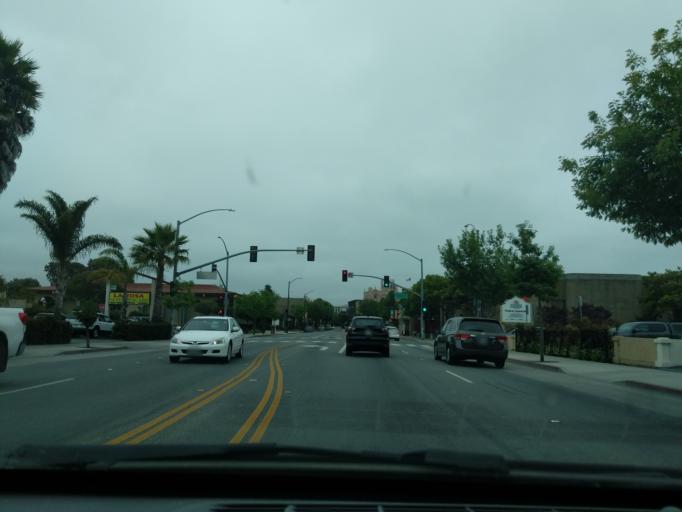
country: US
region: California
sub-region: Santa Cruz County
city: Watsonville
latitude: 36.9135
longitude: -121.7601
